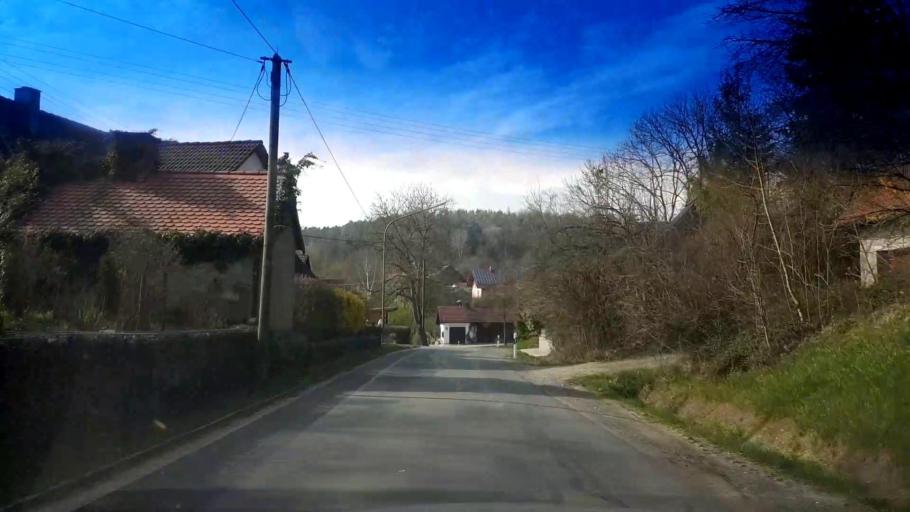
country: DE
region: Bavaria
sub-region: Upper Franconia
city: Harsdorf
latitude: 50.0352
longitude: 11.5837
